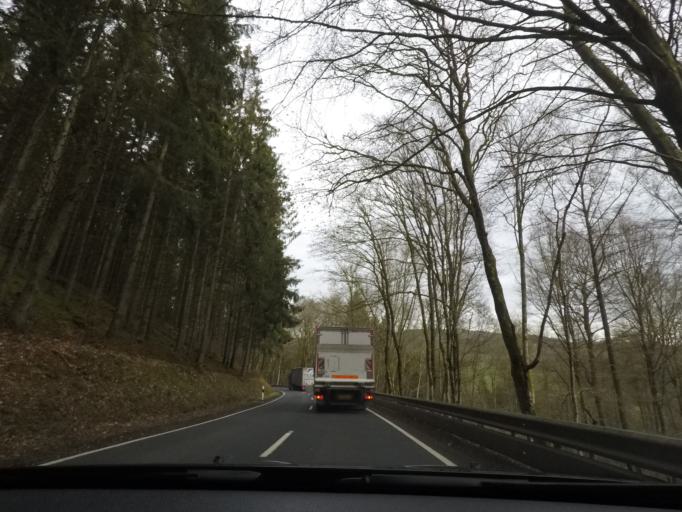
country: LU
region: Diekirch
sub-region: Canton de Wiltz
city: Winseler
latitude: 49.9833
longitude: 5.8559
